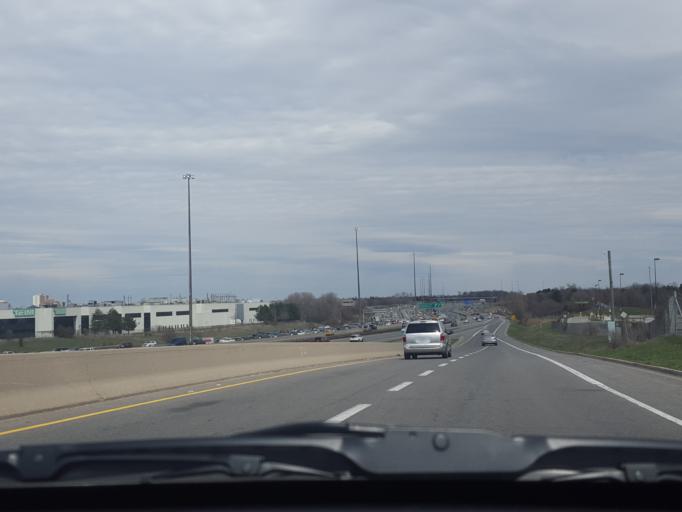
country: CA
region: Ontario
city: Scarborough
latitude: 43.7857
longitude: -79.2319
